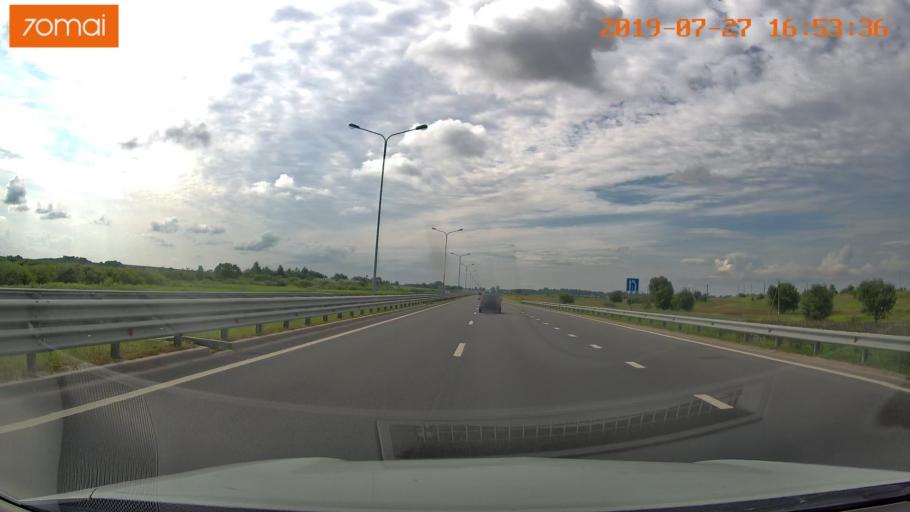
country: RU
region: Kaliningrad
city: Bol'shoe Isakovo
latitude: 54.6888
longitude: 20.8293
